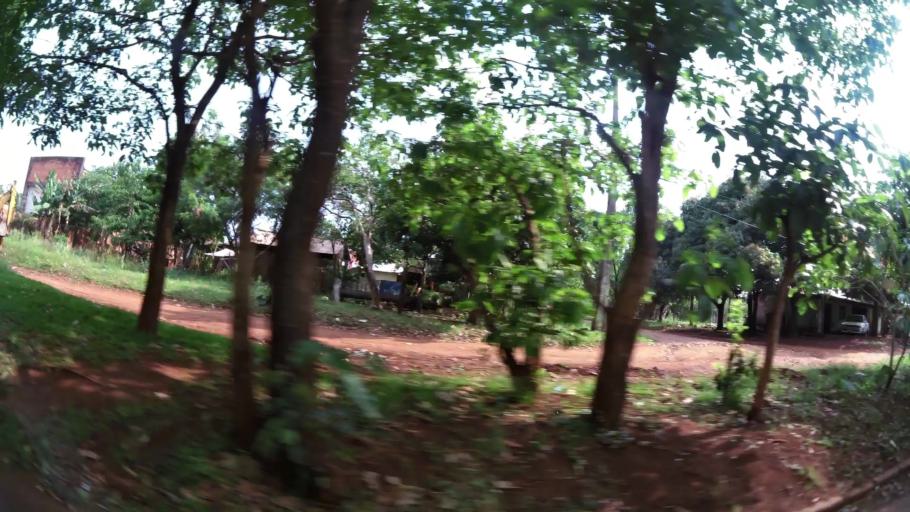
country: PY
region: Alto Parana
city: Ciudad del Este
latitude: -25.4866
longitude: -54.6410
